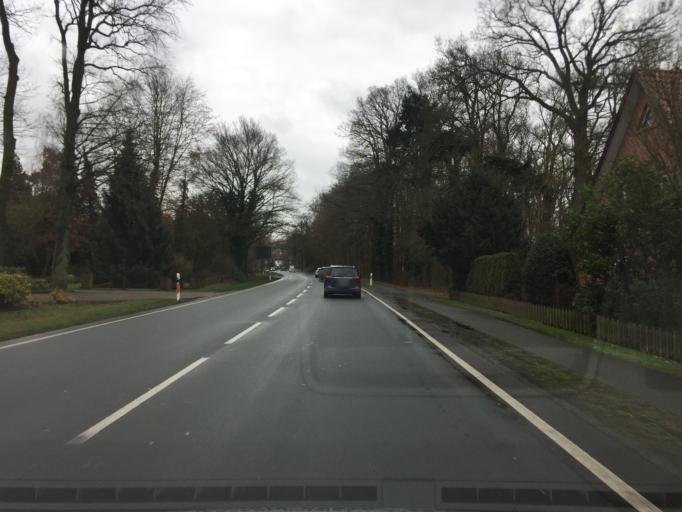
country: DE
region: Lower Saxony
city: Sulingen
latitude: 52.6967
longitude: 8.7771
